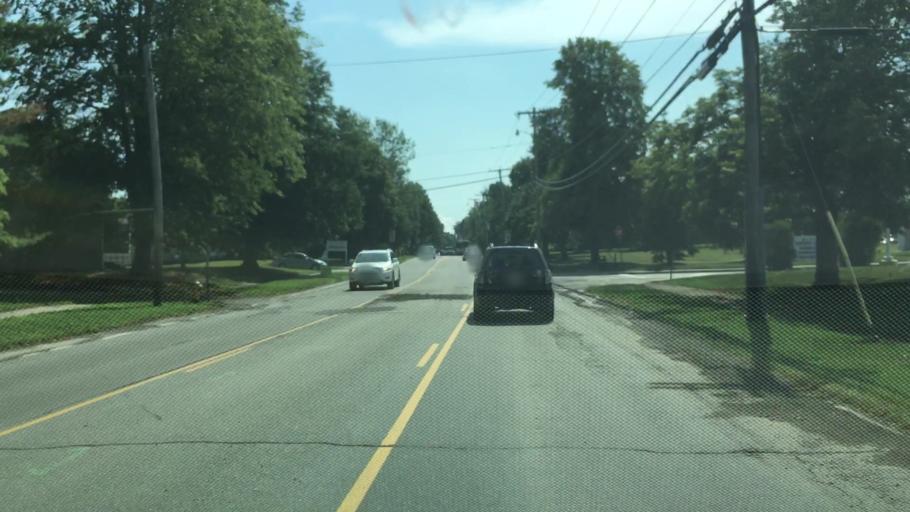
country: US
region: Maine
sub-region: Penobscot County
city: Brewer
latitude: 44.8205
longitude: -68.7619
